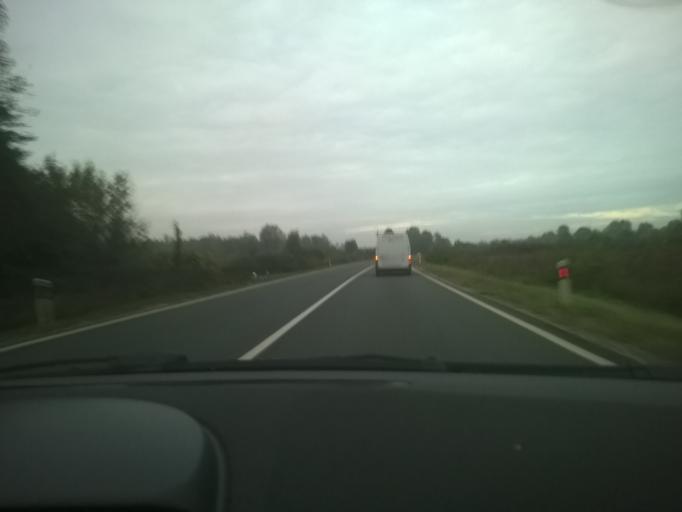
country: HR
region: Zagrebacka
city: Jakovlje
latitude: 45.9676
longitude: 15.8468
